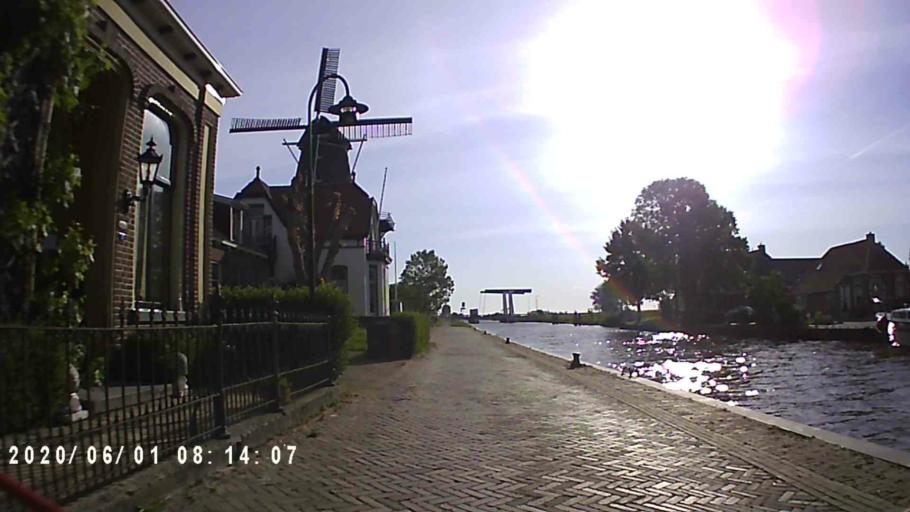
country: NL
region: Friesland
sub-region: Gemeente Ferwerderadiel
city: Burdaard
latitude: 53.2956
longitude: 5.8810
